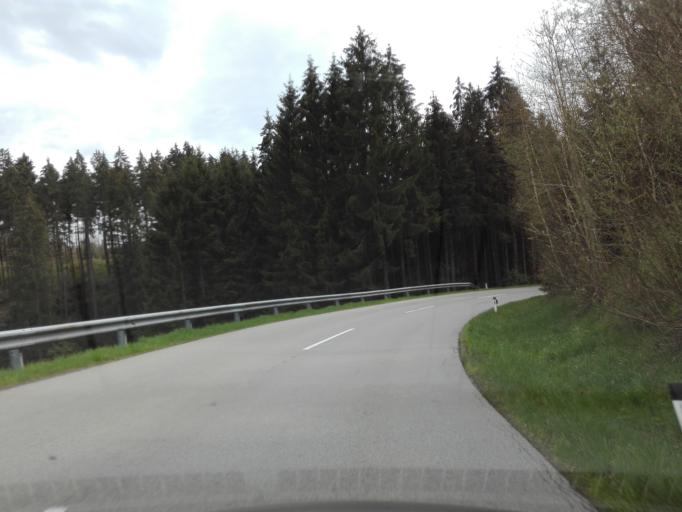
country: AT
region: Upper Austria
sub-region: Politischer Bezirk Rohrbach
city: Atzesberg
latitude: 48.5420
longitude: 13.9537
